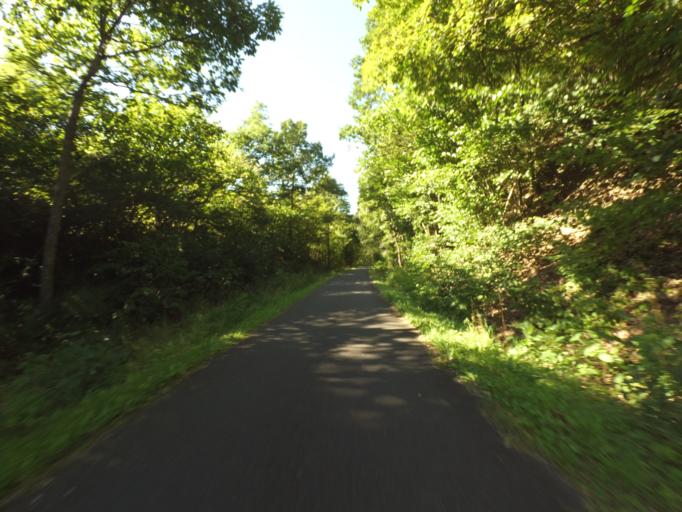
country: DE
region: Rheinland-Pfalz
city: Mehren
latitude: 50.1748
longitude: 6.8717
